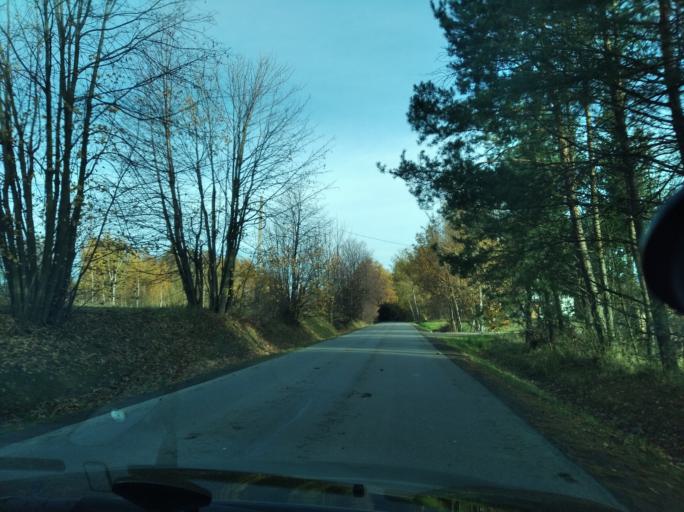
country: PL
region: Subcarpathian Voivodeship
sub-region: Powiat rzeszowski
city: Siedliska
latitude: 49.9429
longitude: 21.9784
